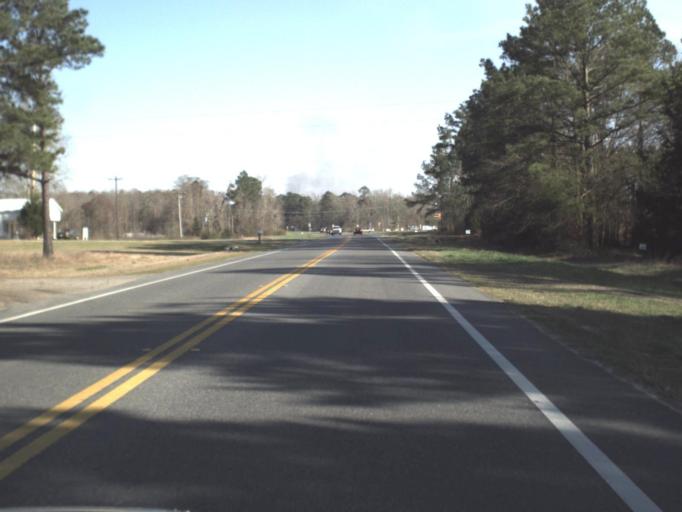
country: US
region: Florida
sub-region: Jackson County
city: Marianna
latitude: 30.7243
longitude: -85.0818
